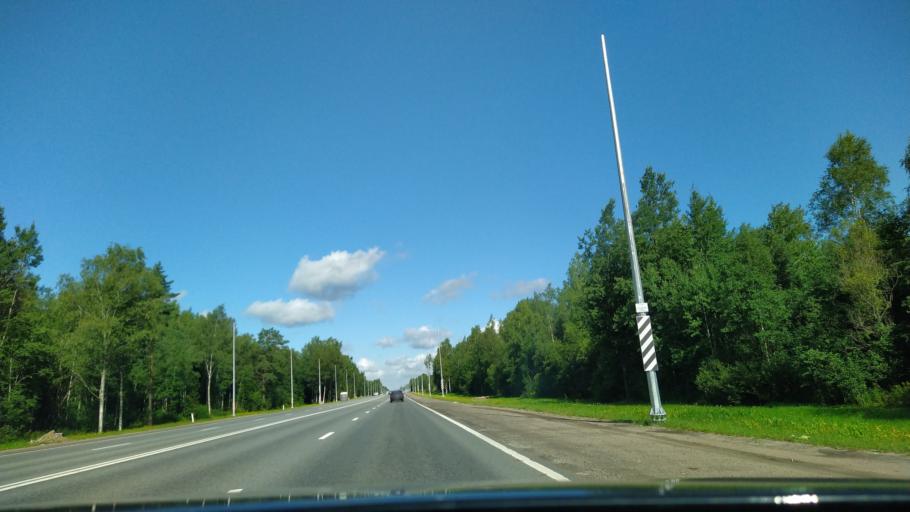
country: RU
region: Leningrad
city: Tosno
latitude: 59.5739
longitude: 30.8173
